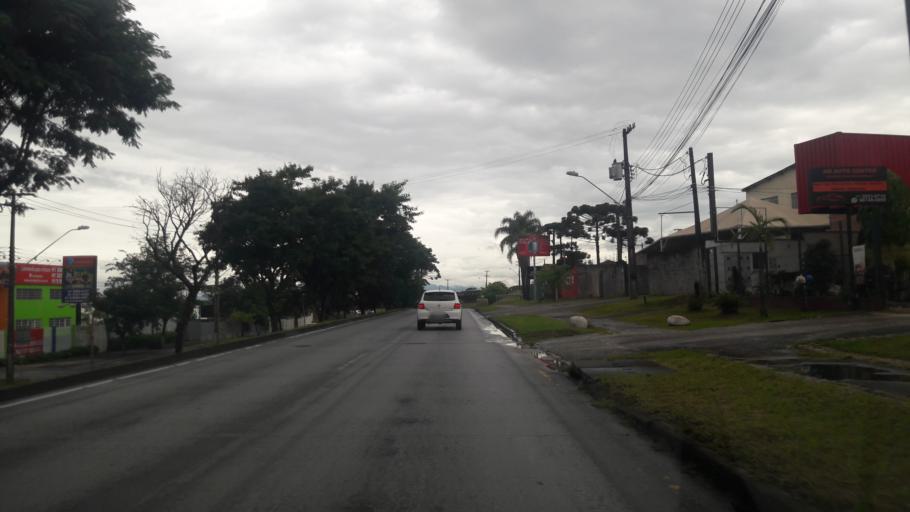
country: BR
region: Parana
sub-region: Pinhais
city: Pinhais
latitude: -25.3871
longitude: -49.2102
